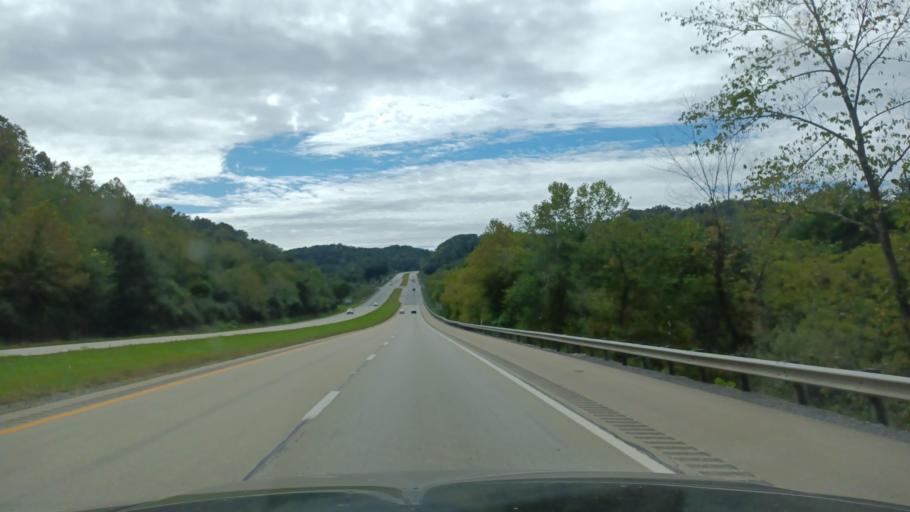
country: US
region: West Virginia
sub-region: Doddridge County
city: West Union
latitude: 39.2925
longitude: -80.7643
